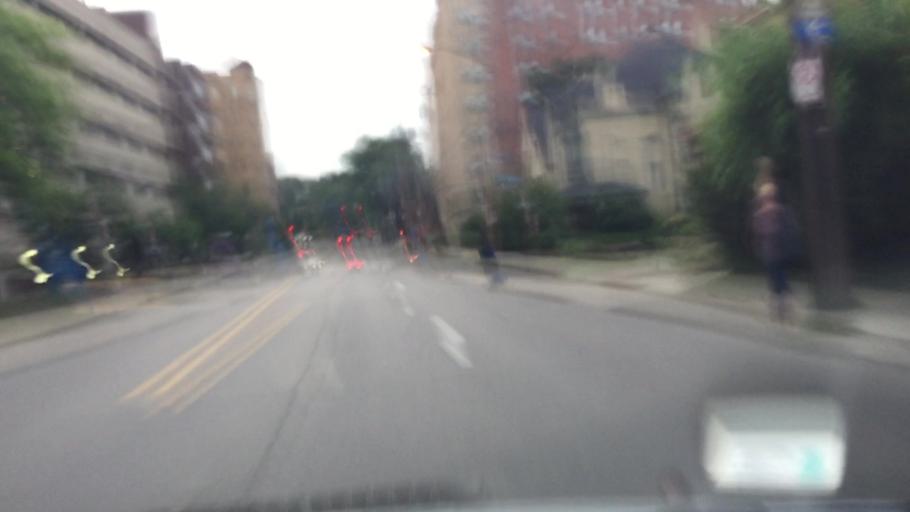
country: US
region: Pennsylvania
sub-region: Allegheny County
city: Bloomfield
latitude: 40.4546
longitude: -79.9378
